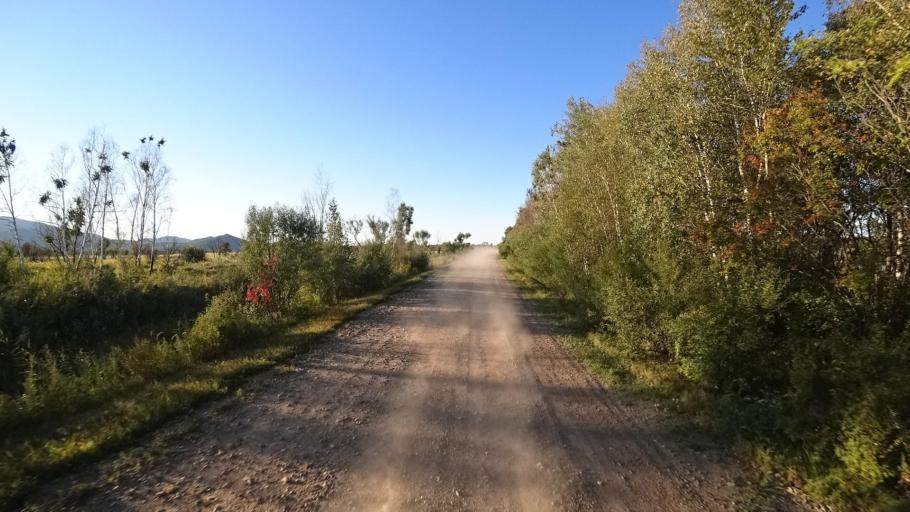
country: RU
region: Primorskiy
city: Kirovskiy
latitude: 44.8090
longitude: 133.6167
